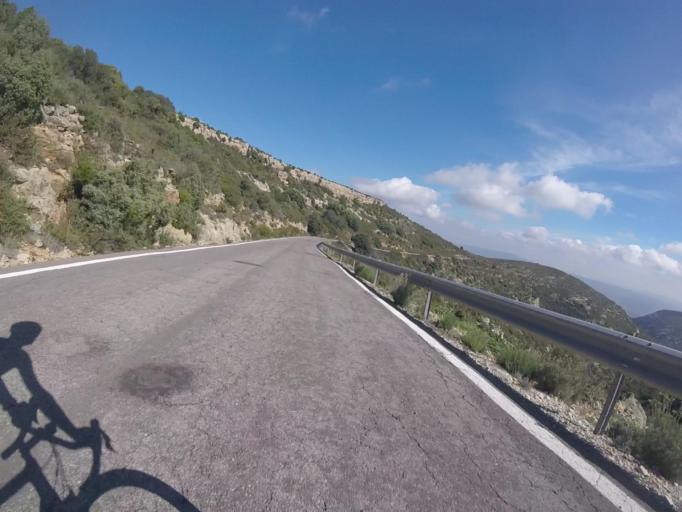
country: ES
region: Valencia
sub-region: Provincia de Castello
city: Albocasser
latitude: 40.3363
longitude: 0.0429
